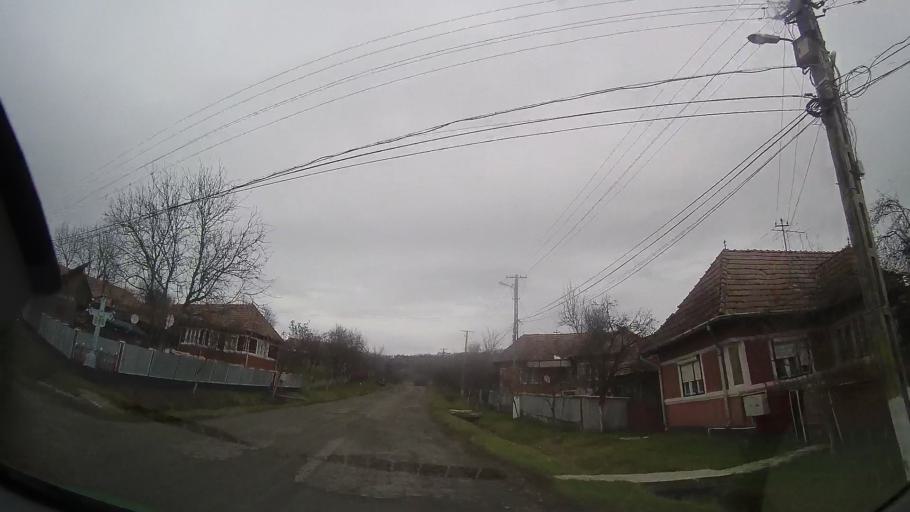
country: RO
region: Mures
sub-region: Comuna Bala
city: Bala
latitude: 46.7100
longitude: 24.5015
